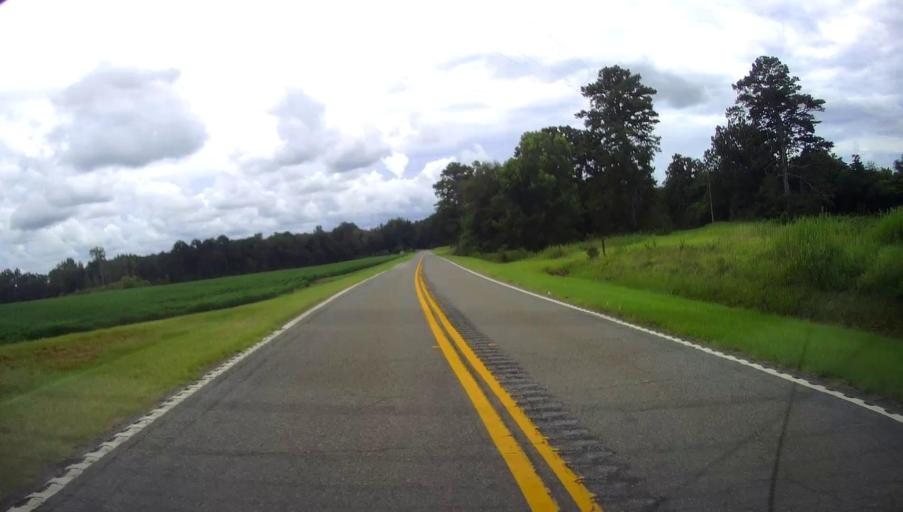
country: US
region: Georgia
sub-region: Dooly County
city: Unadilla
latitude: 32.2886
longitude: -83.8273
